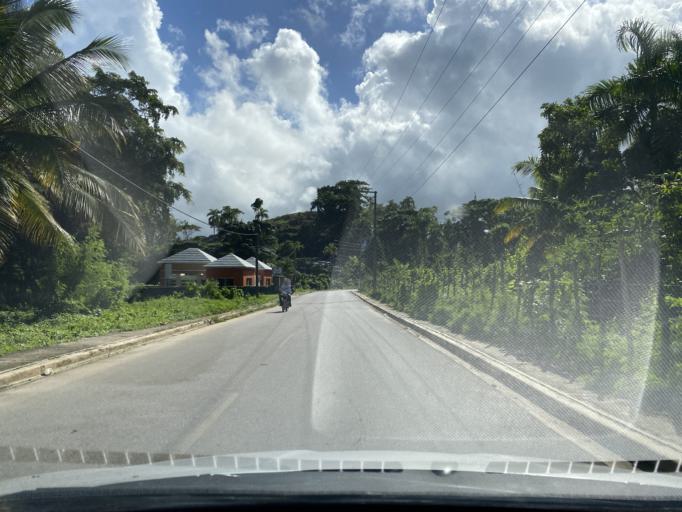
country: DO
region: Samana
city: Las Terrenas
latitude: 19.3193
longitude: -69.5295
